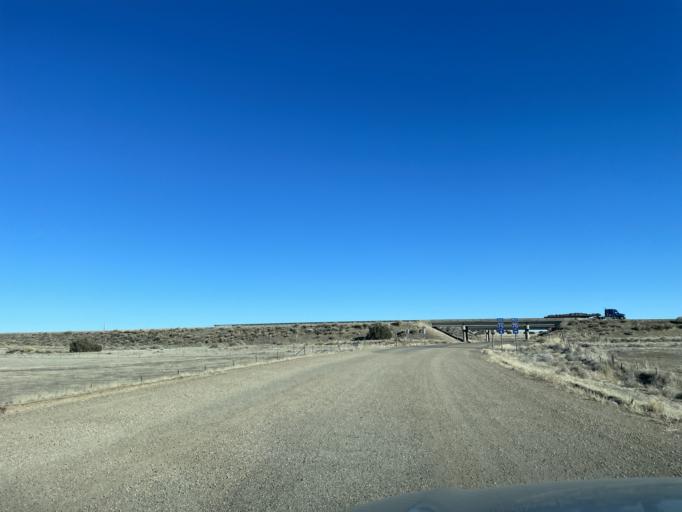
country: US
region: Colorado
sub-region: Mesa County
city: Loma
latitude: 39.1754
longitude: -109.1296
